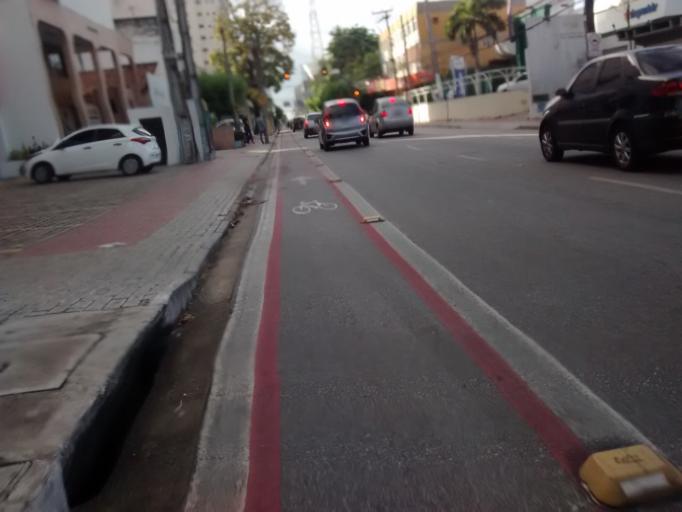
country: BR
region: Ceara
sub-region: Fortaleza
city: Fortaleza
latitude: -3.7448
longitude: -38.5044
